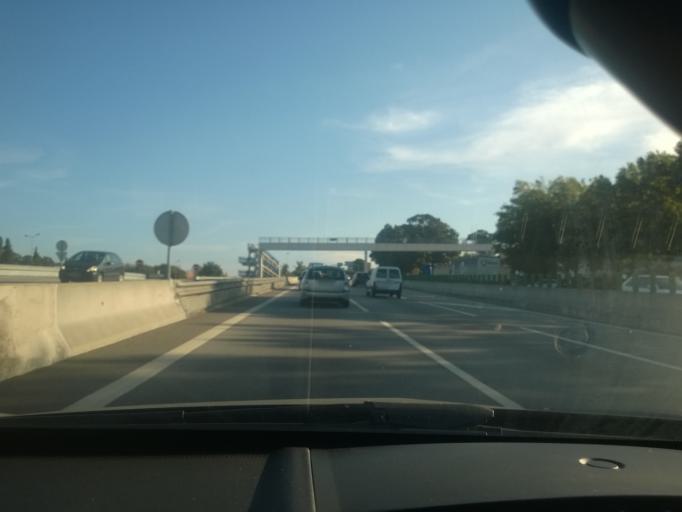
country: PT
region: Porto
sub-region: Maia
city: Leca do Bailio
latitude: 41.1987
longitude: -8.6275
